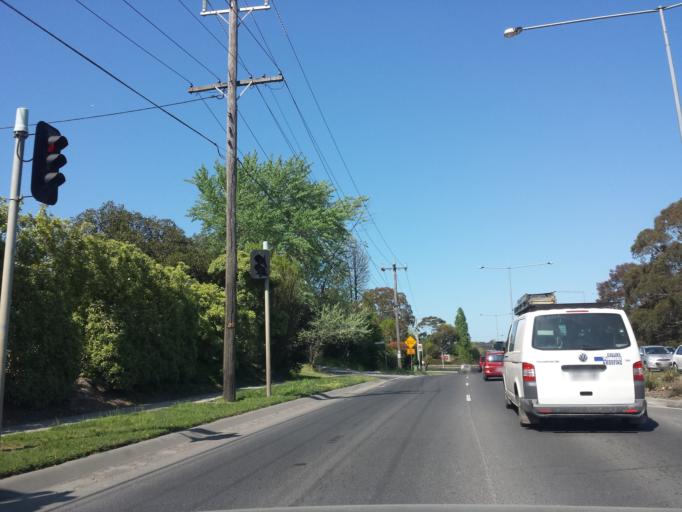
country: AU
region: Victoria
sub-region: Yarra Ranges
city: Lilydale
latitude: -37.7592
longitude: 145.3545
